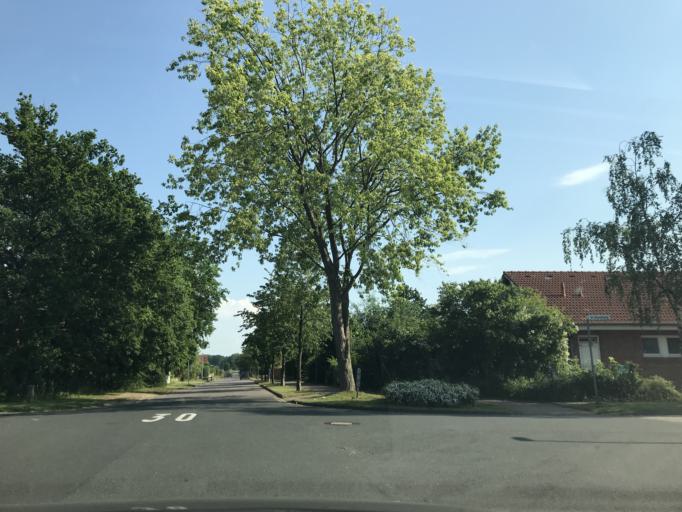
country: DE
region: Lower Saxony
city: Sehnde
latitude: 52.3436
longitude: 9.9377
